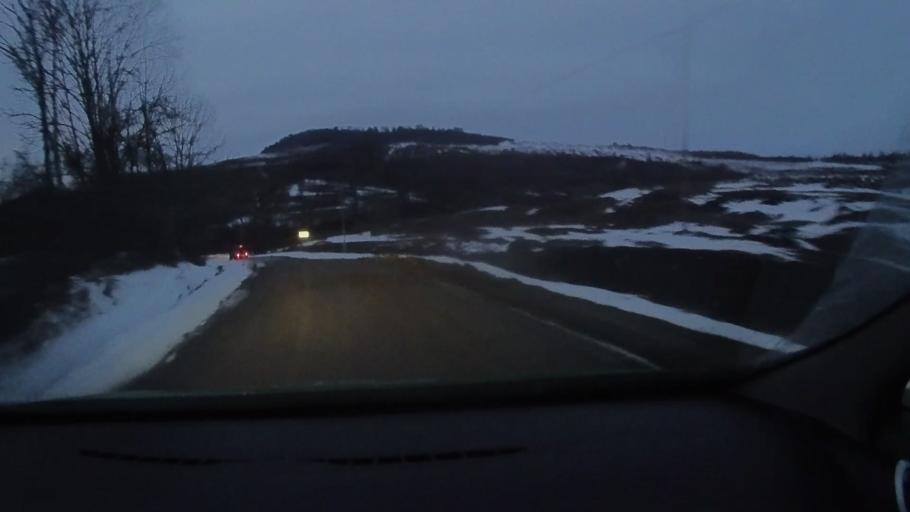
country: RO
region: Harghita
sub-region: Comuna Darjiu
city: Darjiu
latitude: 46.1763
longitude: 25.2425
